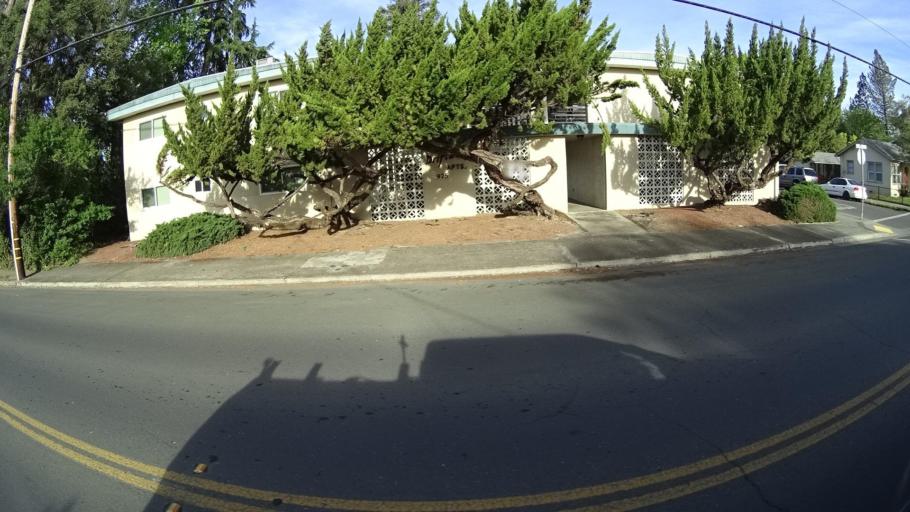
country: US
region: California
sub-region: Lake County
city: Lakeport
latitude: 39.0480
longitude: -122.9161
